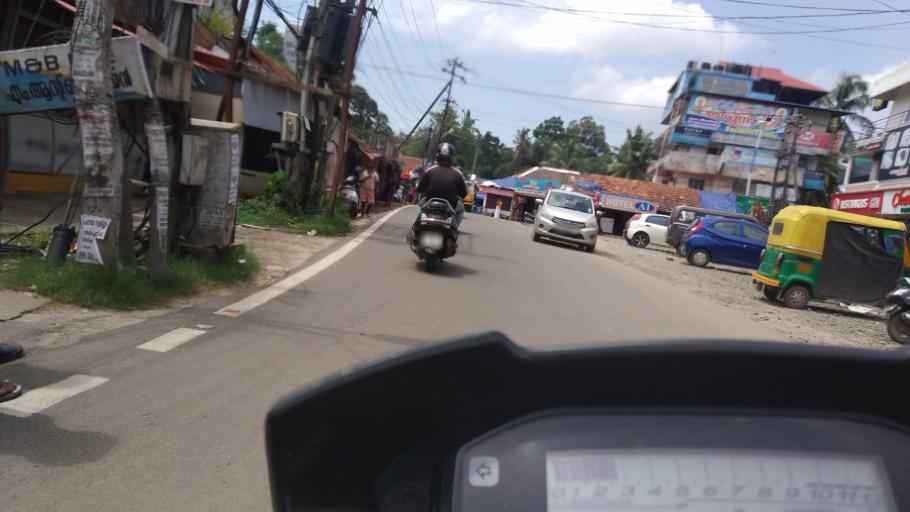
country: IN
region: Kerala
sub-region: Ernakulam
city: Cochin
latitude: 9.9863
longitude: 76.3105
